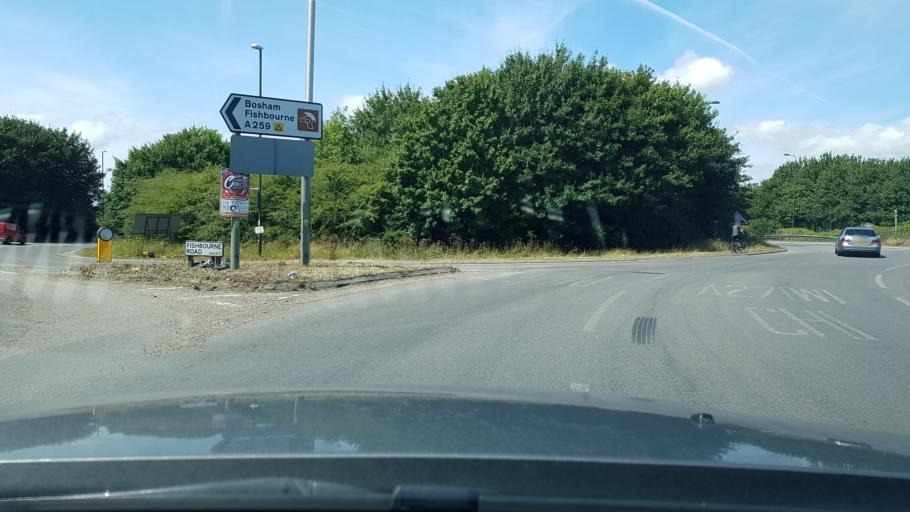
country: GB
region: England
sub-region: West Sussex
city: Chichester
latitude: 50.8326
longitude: -0.7992
